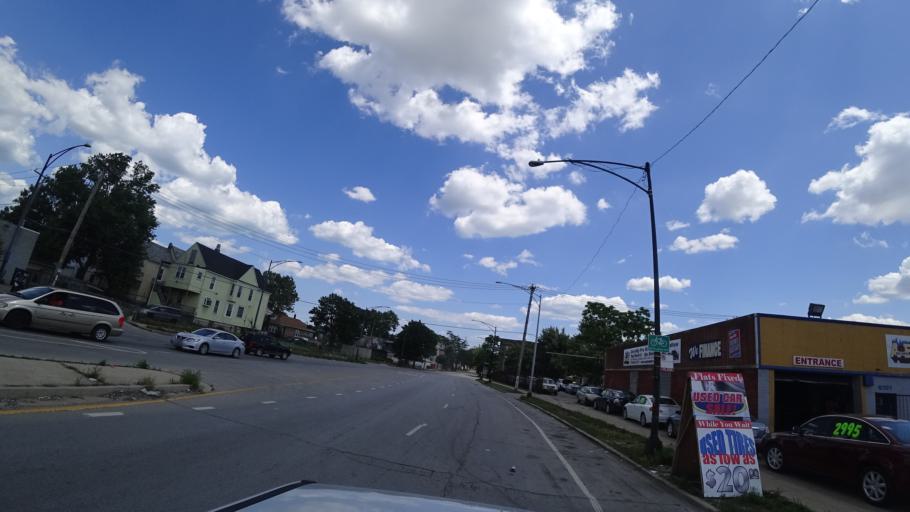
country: US
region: Illinois
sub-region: Cook County
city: Chicago
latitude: 41.7727
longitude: -87.6248
